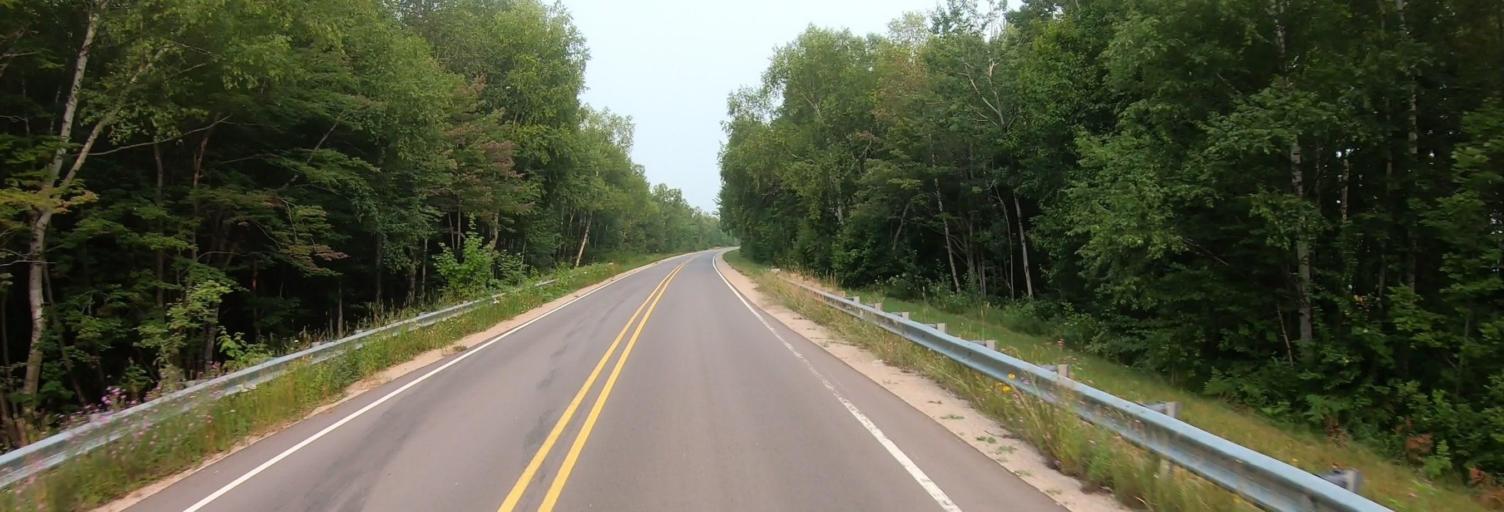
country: US
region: Michigan
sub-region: Luce County
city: Newberry
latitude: 46.4789
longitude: -85.0135
